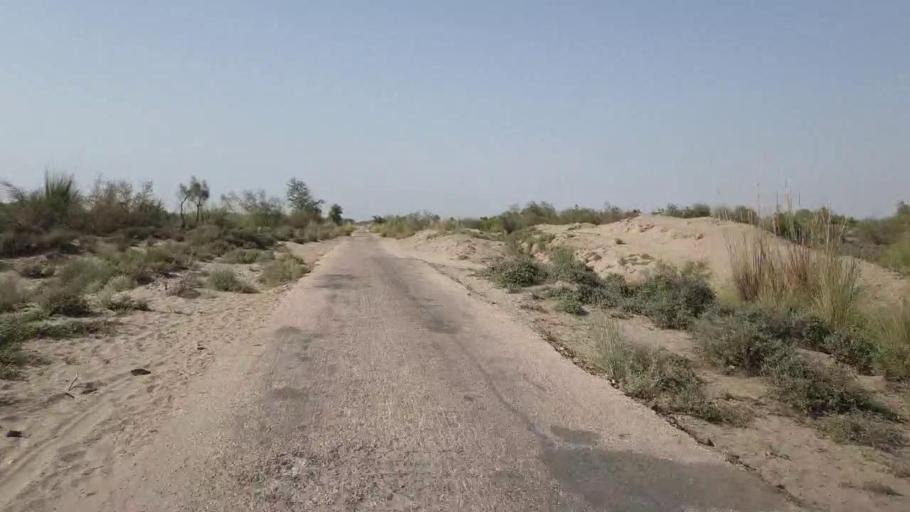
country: PK
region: Sindh
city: Jam Sahib
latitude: 26.5871
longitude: 68.9215
